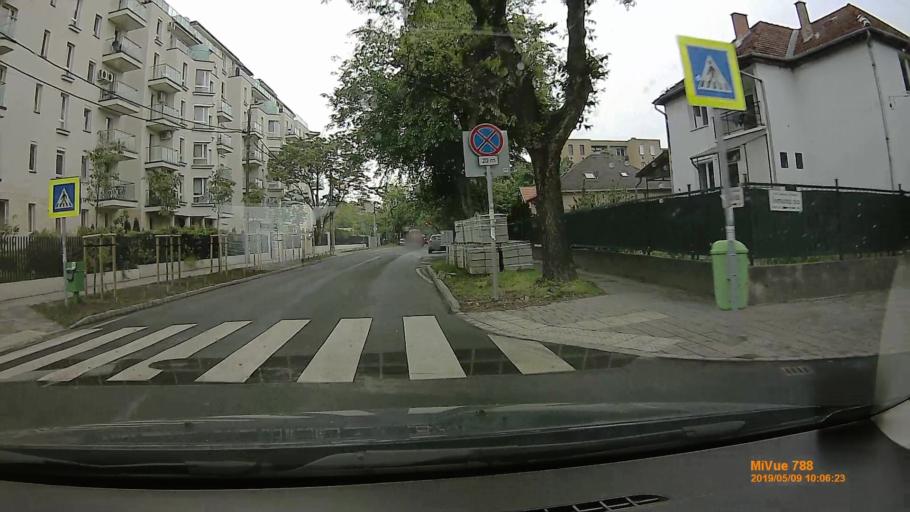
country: HU
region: Budapest
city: Budapest XIV. keruelet
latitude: 47.5335
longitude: 19.1082
